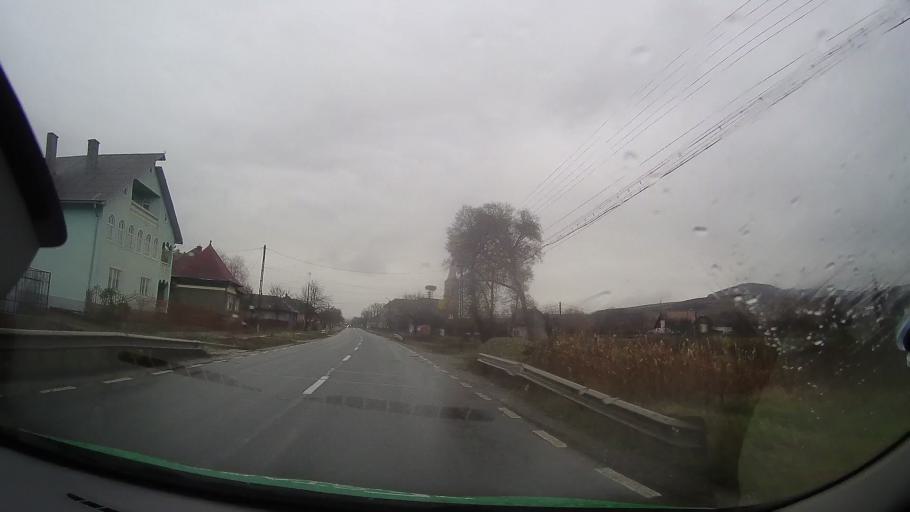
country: RO
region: Bistrita-Nasaud
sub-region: Comuna Galatii Bistritei
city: Galatii Bistritei
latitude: 46.9722
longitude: 24.4332
